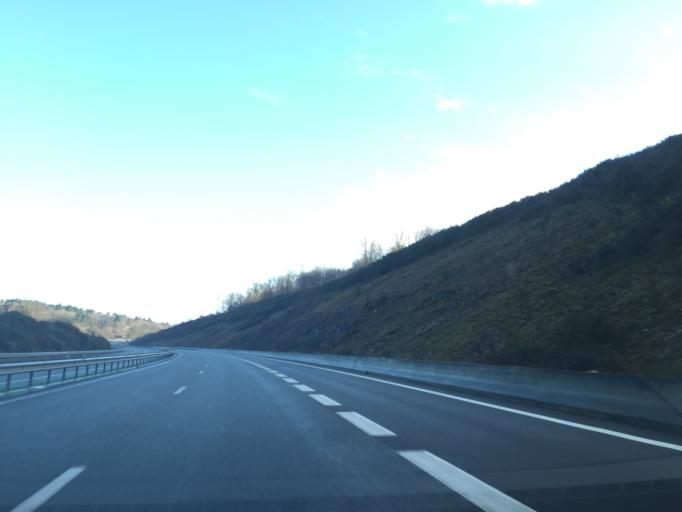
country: FR
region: Aquitaine
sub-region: Departement de la Dordogne
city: Terrasson-Lavilledieu
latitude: 45.1554
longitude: 1.2160
